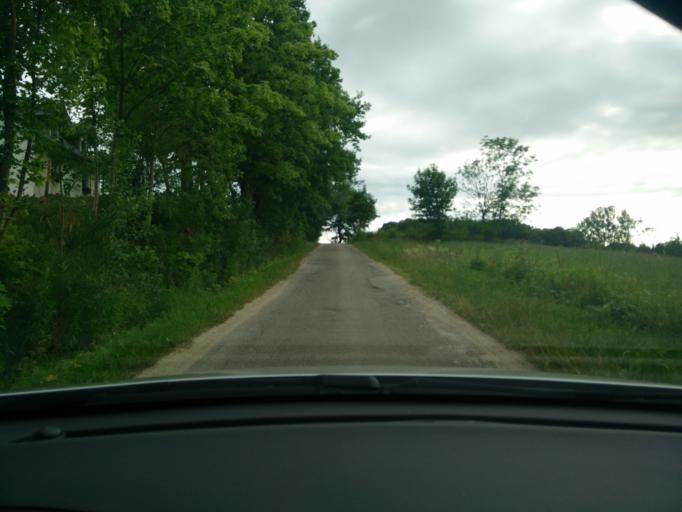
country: PL
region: Pomeranian Voivodeship
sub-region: Powiat pucki
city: Mrzezino
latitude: 54.6629
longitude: 18.4552
